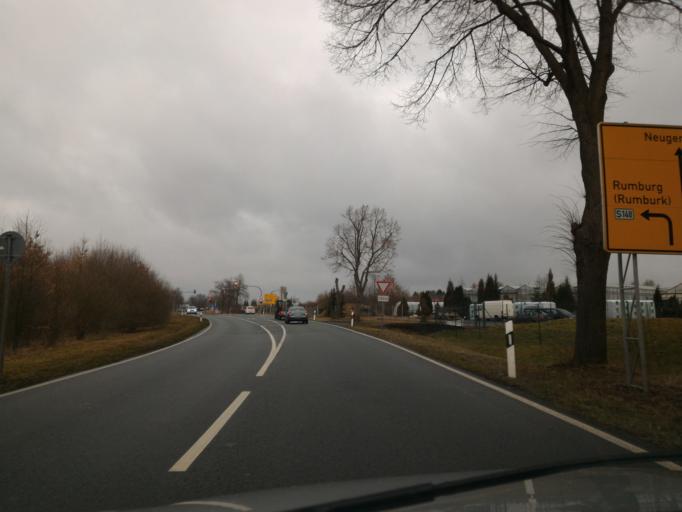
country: DE
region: Saxony
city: Neugersdorf
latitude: 50.9786
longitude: 14.6327
